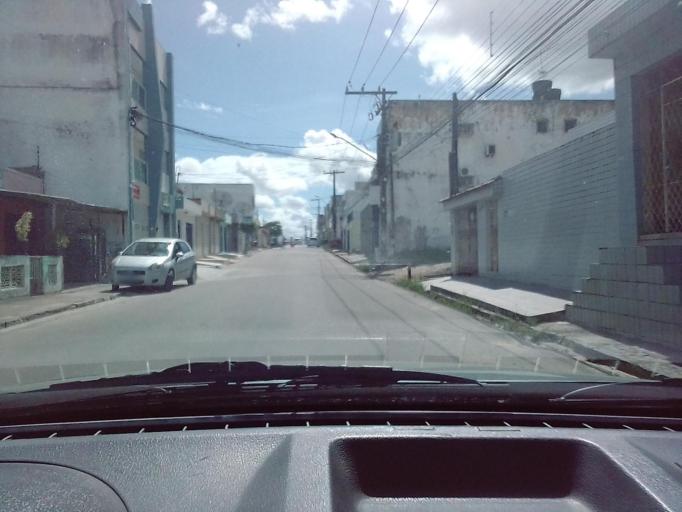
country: BR
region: Pernambuco
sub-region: Vitoria De Santo Antao
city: Vitoria de Santo Antao
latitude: -8.1181
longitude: -35.3075
